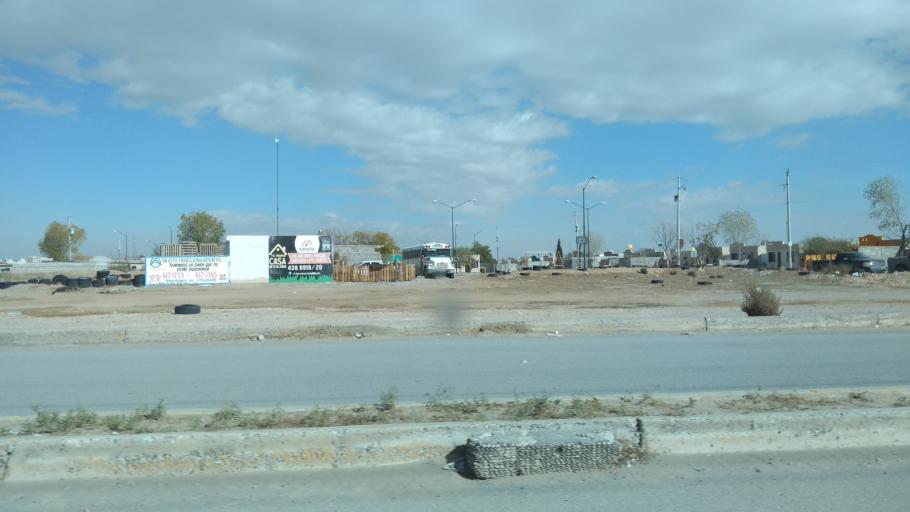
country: US
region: Texas
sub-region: El Paso County
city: San Elizario
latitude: 31.5747
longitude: -106.3444
